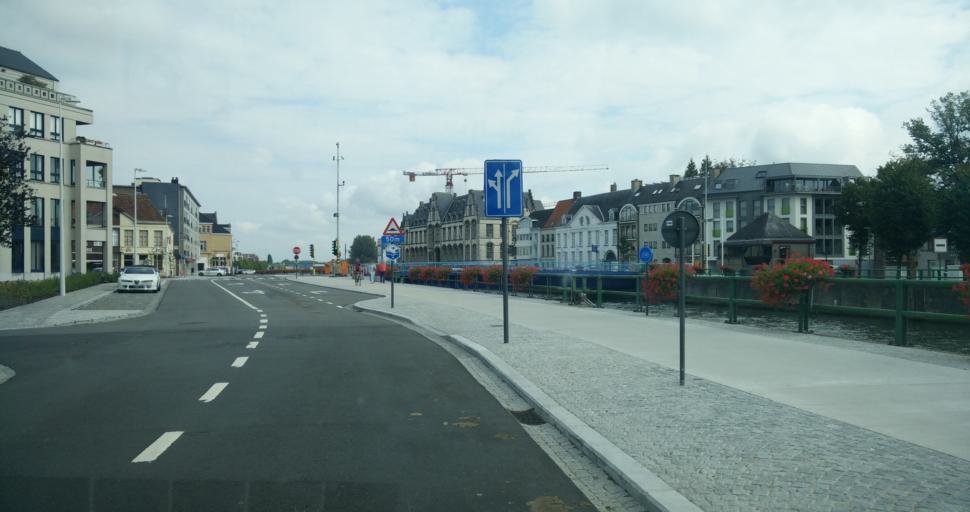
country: BE
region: Flanders
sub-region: Provincie Oost-Vlaanderen
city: Oudenaarde
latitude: 50.8419
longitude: 3.6080
